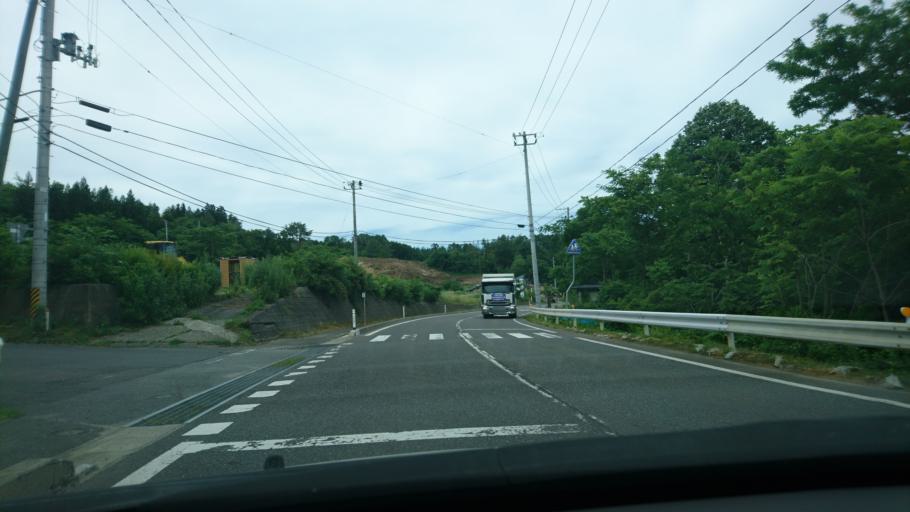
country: JP
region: Iwate
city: Miyako
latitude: 39.9409
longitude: 141.8403
